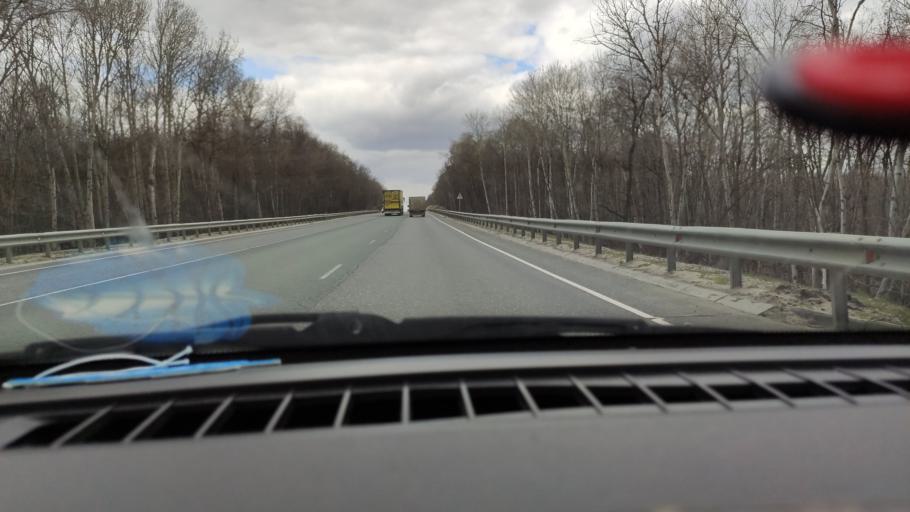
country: RU
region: Saratov
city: Vol'sk
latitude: 52.1077
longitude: 47.4093
